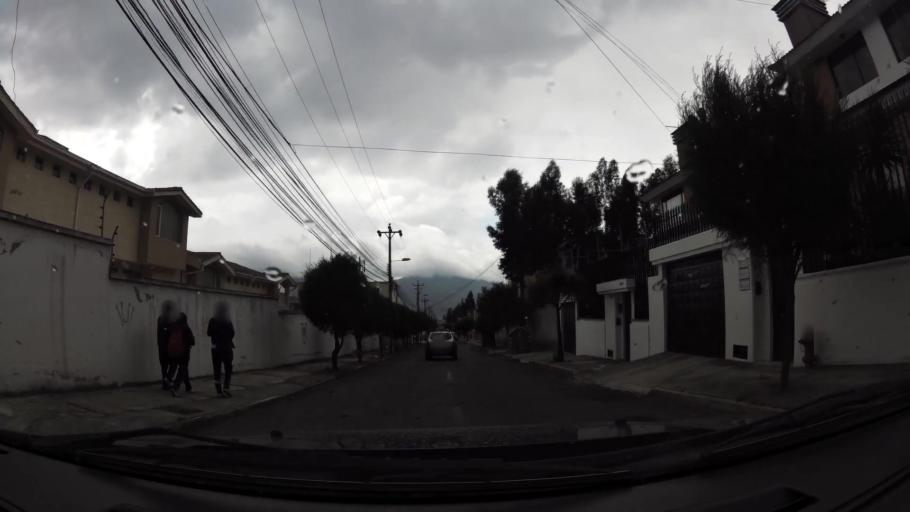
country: EC
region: Pichincha
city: Quito
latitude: -0.1066
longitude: -78.4810
